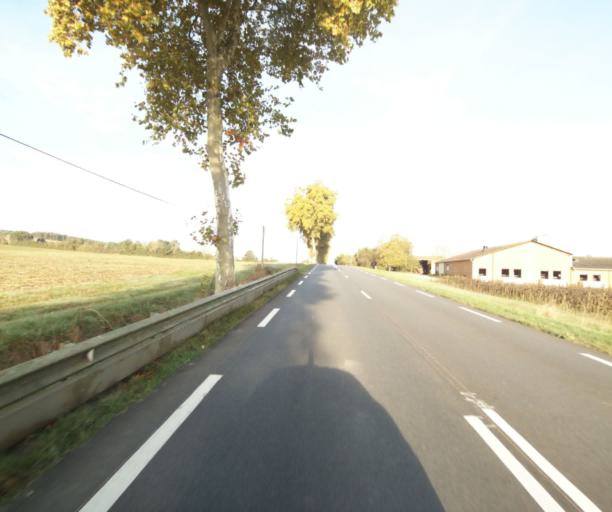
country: FR
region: Midi-Pyrenees
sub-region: Departement du Tarn-et-Garonne
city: Saint-Nauphary
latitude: 43.9377
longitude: 1.4790
